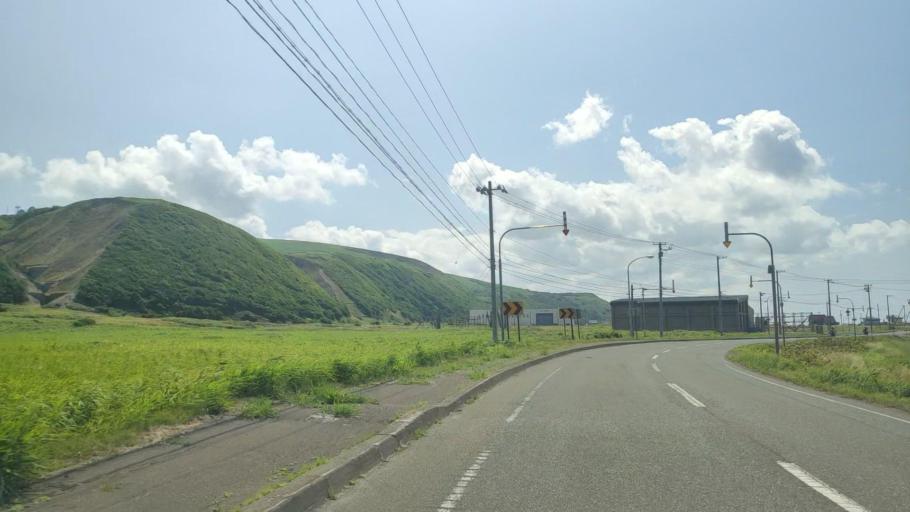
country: JP
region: Hokkaido
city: Wakkanai
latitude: 45.4274
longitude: 141.6383
